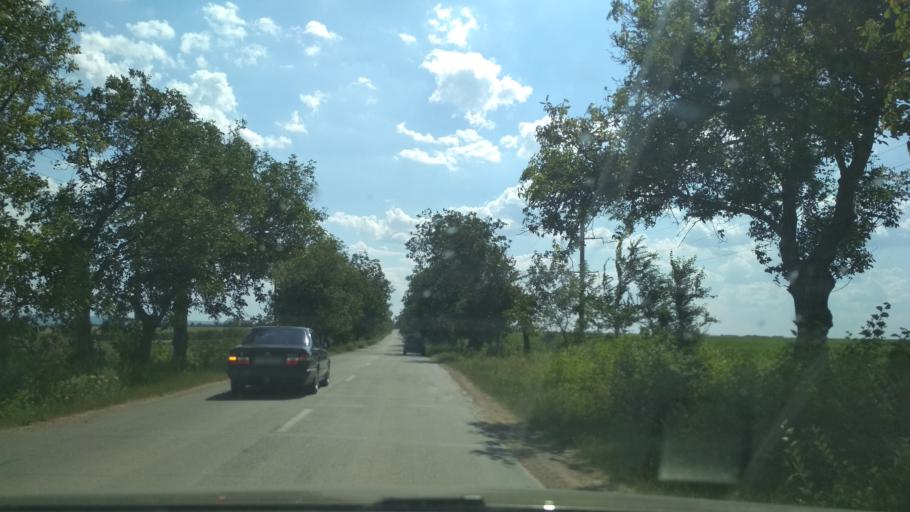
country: MD
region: Criuleni
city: Criuleni
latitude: 47.1681
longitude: 29.1816
